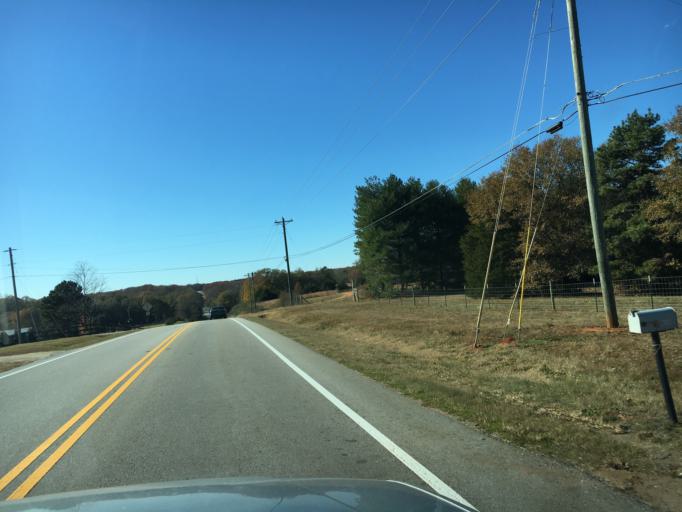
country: US
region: Georgia
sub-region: Hart County
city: Hartwell
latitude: 34.2949
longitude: -83.0085
